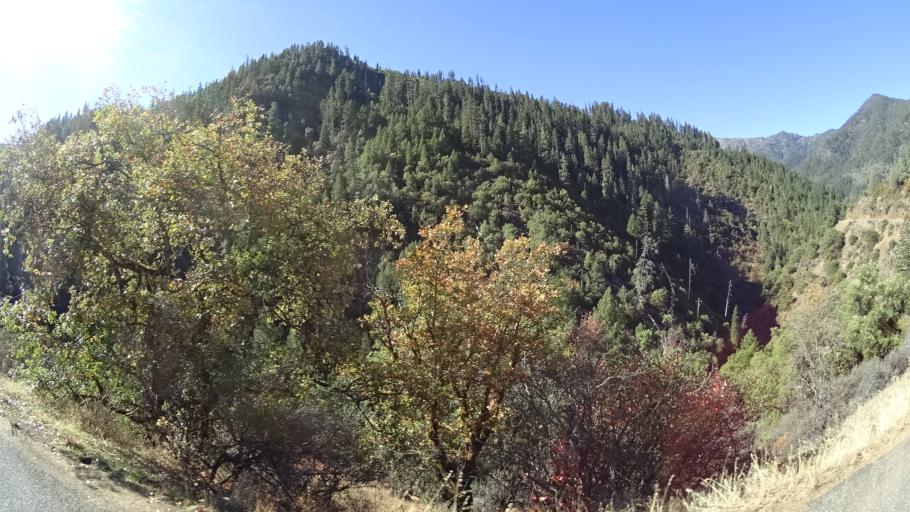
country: US
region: California
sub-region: Humboldt County
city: Willow Creek
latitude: 41.1483
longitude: -123.2045
